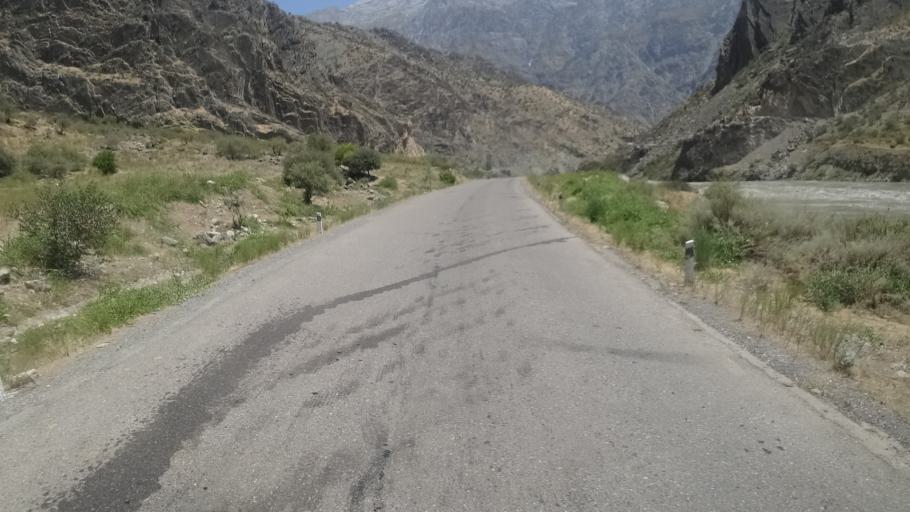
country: AF
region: Badakhshan
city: Deh Khwahan
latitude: 37.9454
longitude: 70.2441
